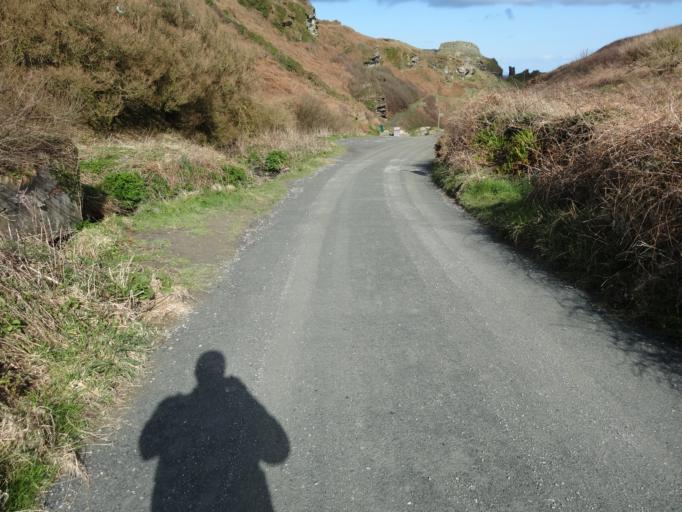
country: GB
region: England
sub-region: Cornwall
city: Tintagel
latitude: 50.6650
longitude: -4.7563
